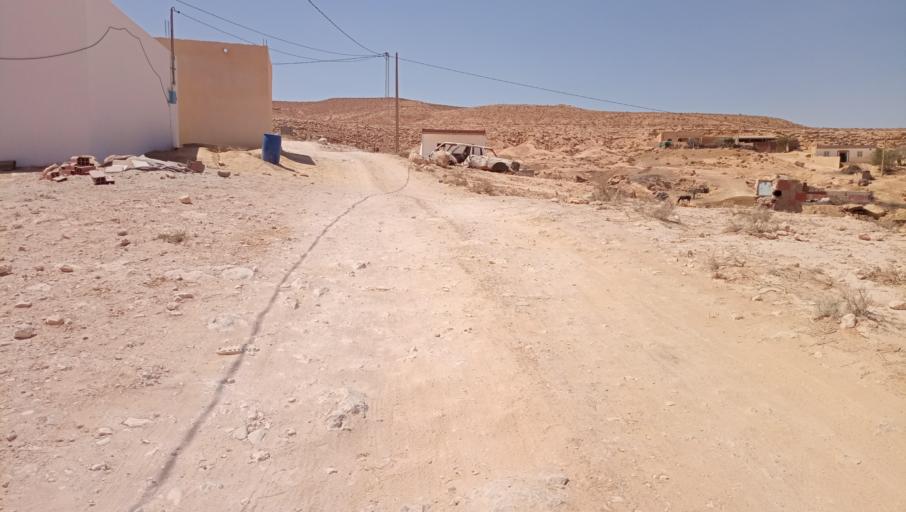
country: TN
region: Tataouine
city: Tataouine
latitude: 32.7823
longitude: 10.5147
